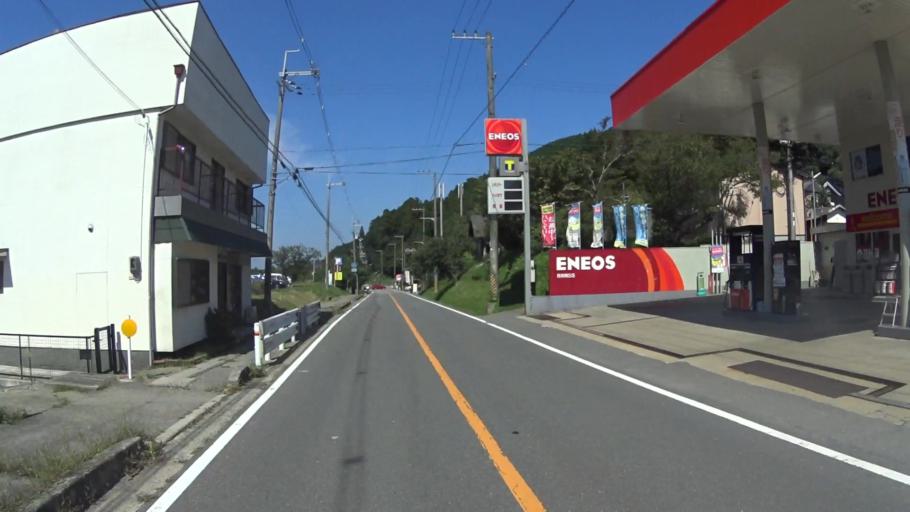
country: JP
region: Kyoto
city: Kameoka
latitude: 34.9420
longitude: 135.4964
